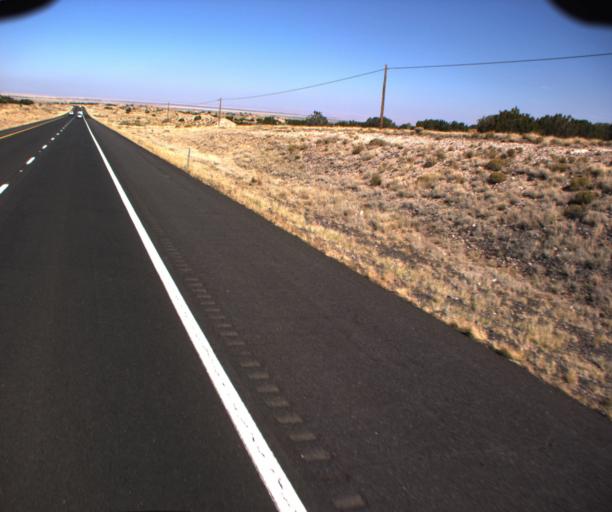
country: US
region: Arizona
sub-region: Coconino County
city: Flagstaff
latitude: 35.5079
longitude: -111.5476
